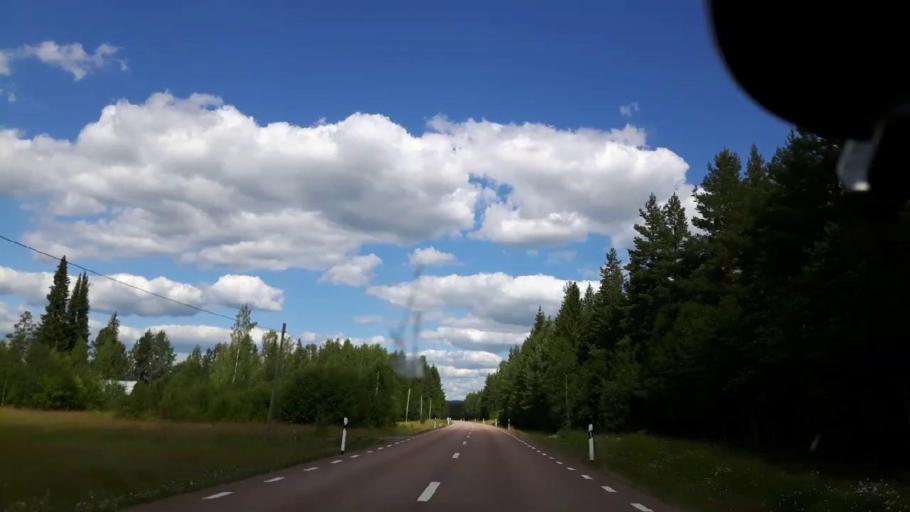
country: SE
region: Jaemtland
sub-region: Ragunda Kommun
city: Hammarstrand
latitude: 62.9078
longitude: 16.7019
